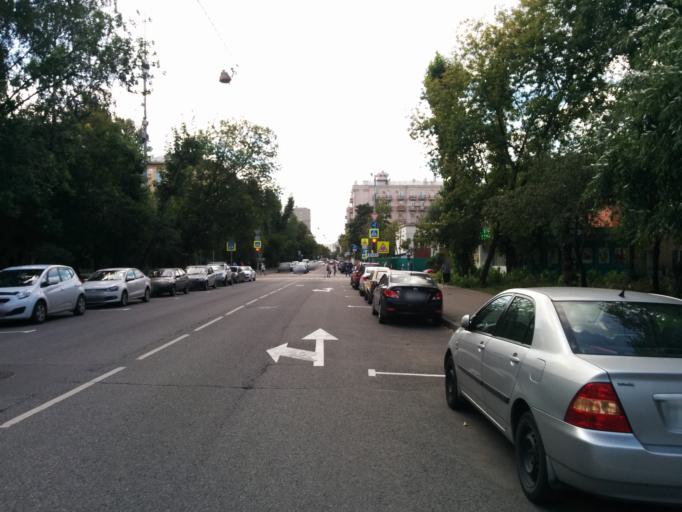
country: RU
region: Moscow
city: Mar'ina Roshcha
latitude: 55.7970
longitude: 37.6127
